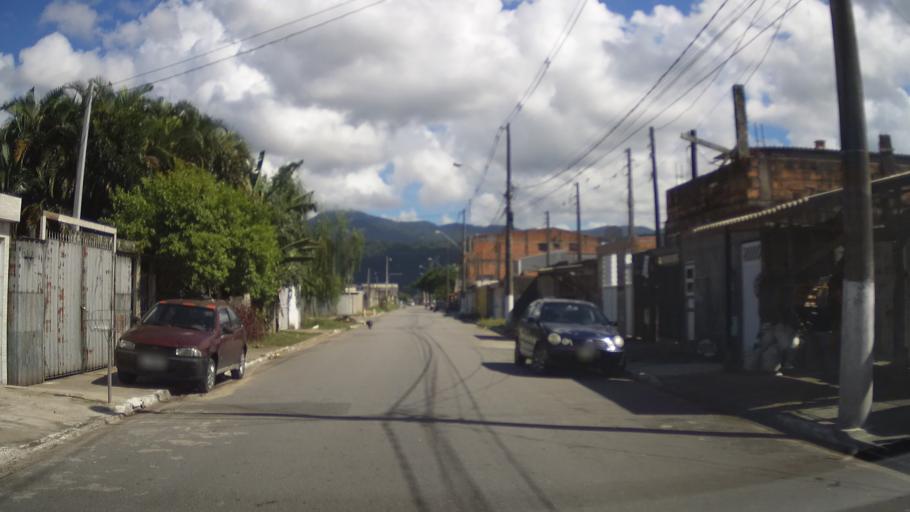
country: BR
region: Sao Paulo
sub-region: Praia Grande
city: Praia Grande
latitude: -24.0245
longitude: -46.5120
